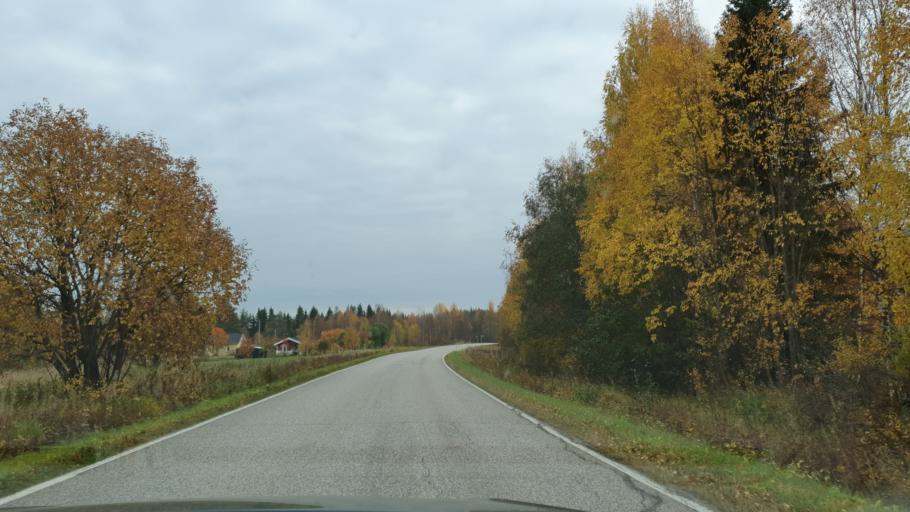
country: FI
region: Kainuu
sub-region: Kajaani
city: Ristijaervi
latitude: 64.4679
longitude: 28.3041
